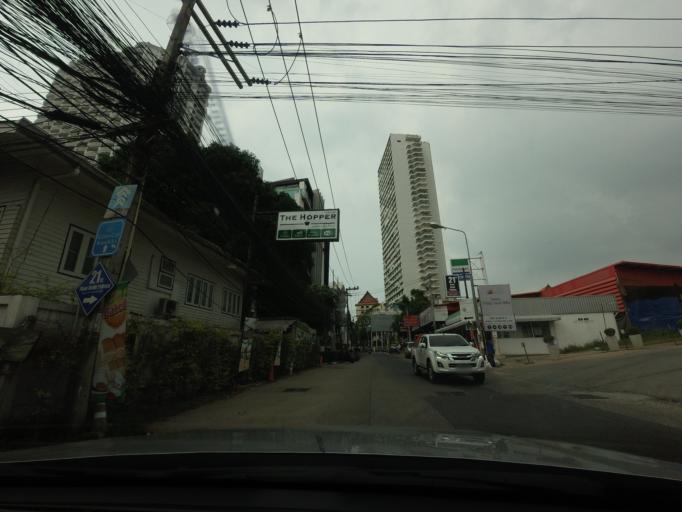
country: TH
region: Chon Buri
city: Phatthaya
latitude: 12.9664
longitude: 100.8855
